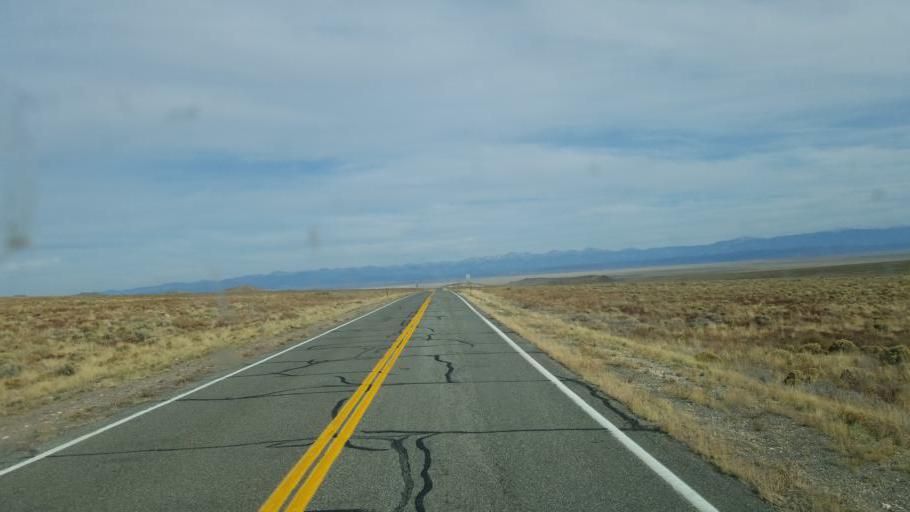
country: US
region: Colorado
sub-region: Conejos County
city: Conejos
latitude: 37.1755
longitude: -105.8041
